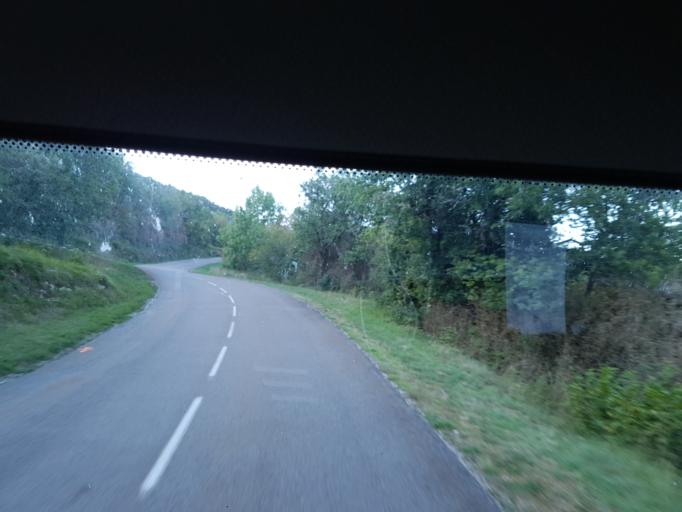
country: FR
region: Franche-Comte
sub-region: Departement du Jura
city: Moirans-en-Montagne
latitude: 46.4155
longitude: 5.6491
